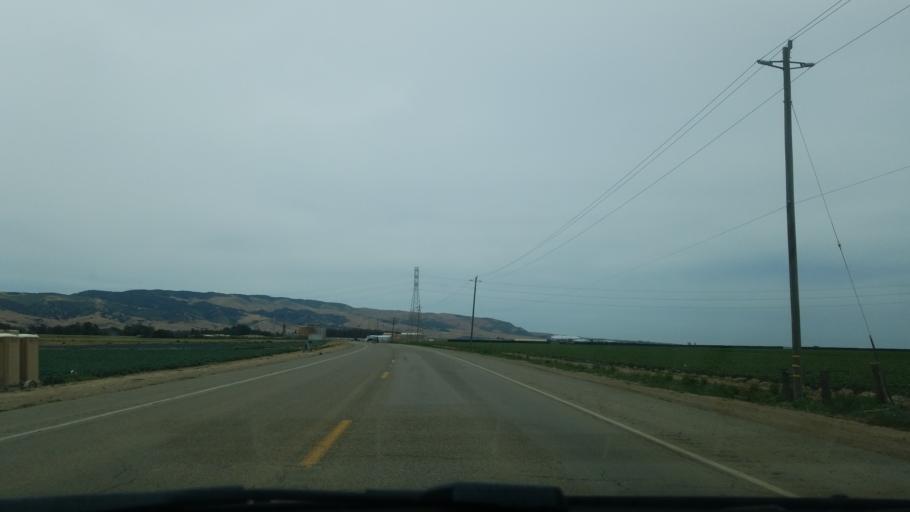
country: US
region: California
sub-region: Santa Barbara County
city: Santa Maria
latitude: 34.9204
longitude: -120.4993
